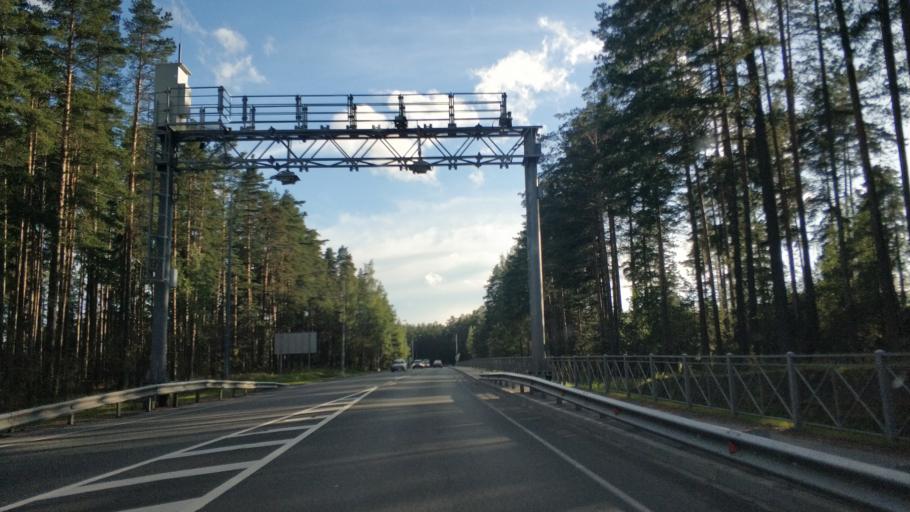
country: RU
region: Leningrad
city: Sapernoye
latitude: 60.7101
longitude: 29.9725
